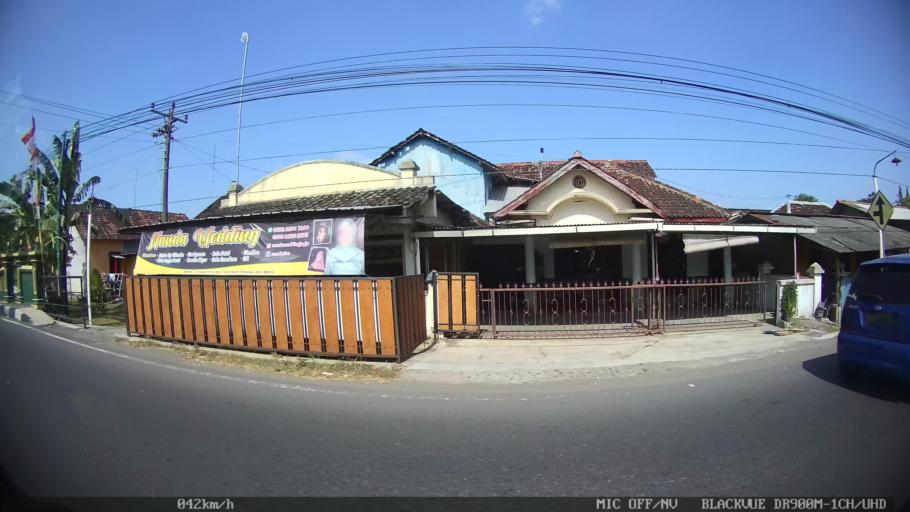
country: ID
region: Daerah Istimewa Yogyakarta
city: Sewon
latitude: -7.8878
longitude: 110.3873
